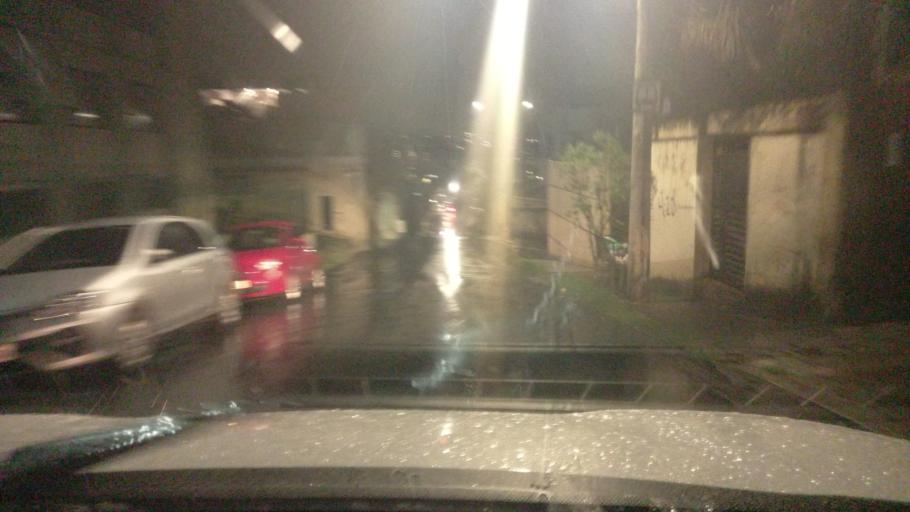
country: BR
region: Minas Gerais
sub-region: Belo Horizonte
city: Belo Horizonte
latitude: -19.9120
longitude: -43.9129
